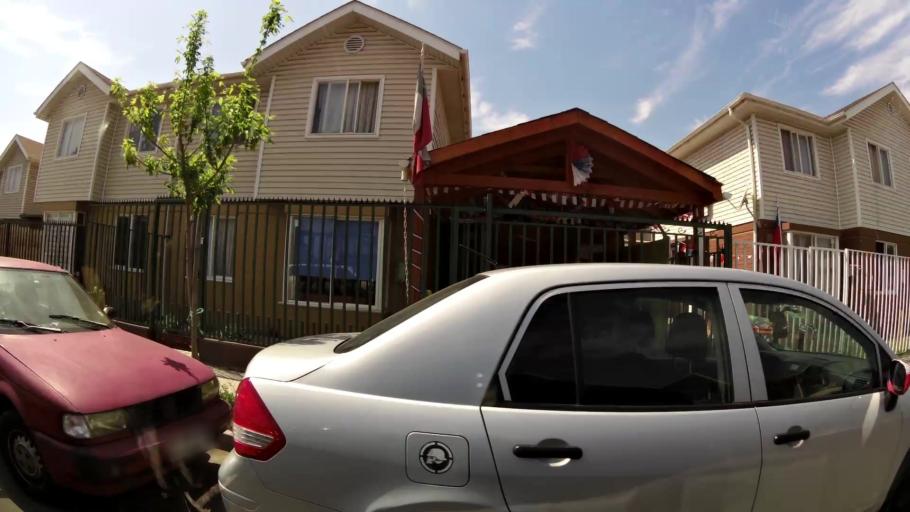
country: CL
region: Santiago Metropolitan
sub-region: Provincia de Cordillera
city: Puente Alto
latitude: -33.5923
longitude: -70.5964
